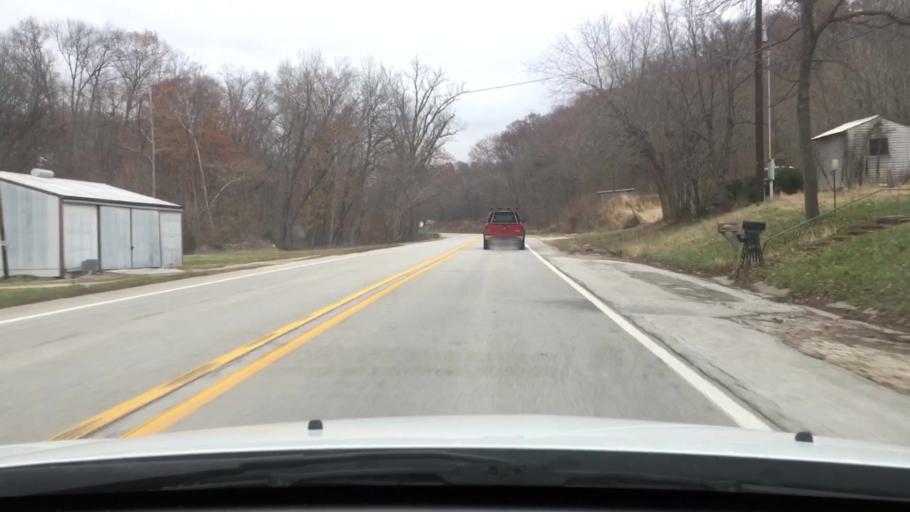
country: US
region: Missouri
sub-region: Pike County
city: Louisiana
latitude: 39.5153
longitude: -90.9629
